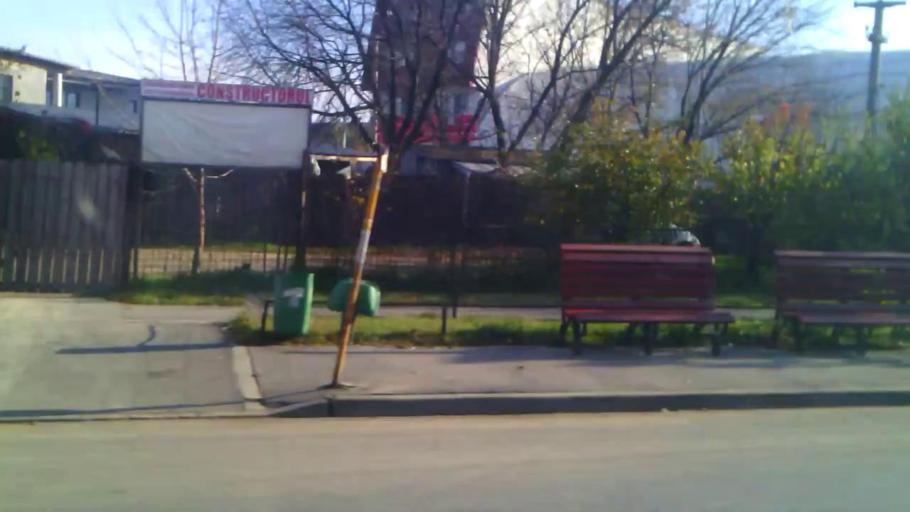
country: RO
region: Ilfov
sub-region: Comuna Popesti-Leordeni
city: Popesti-Leordeni
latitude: 44.3705
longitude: 26.1418
